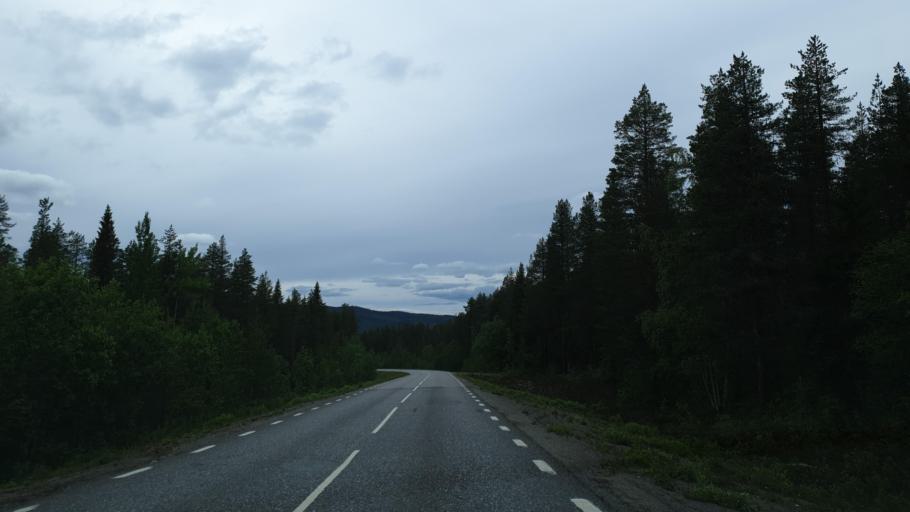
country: SE
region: Vaesterbotten
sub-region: Sorsele Kommun
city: Sorsele
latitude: 65.5442
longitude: 17.4542
